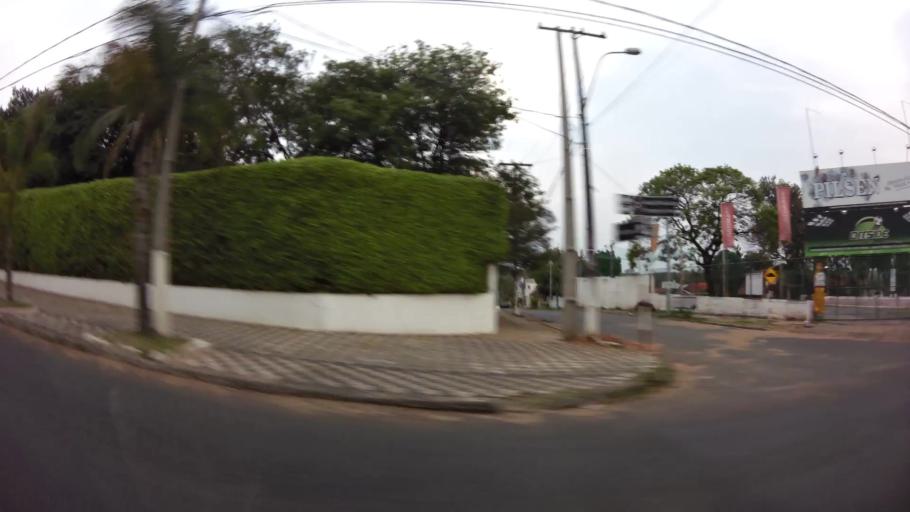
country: PY
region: Central
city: Lambare
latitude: -25.3314
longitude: -57.6292
